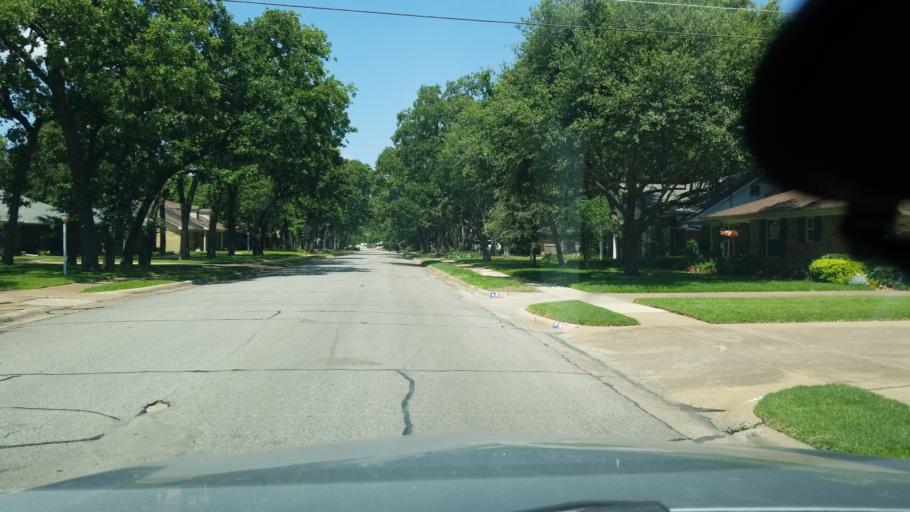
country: US
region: Texas
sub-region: Dallas County
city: Irving
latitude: 32.8338
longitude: -96.9557
